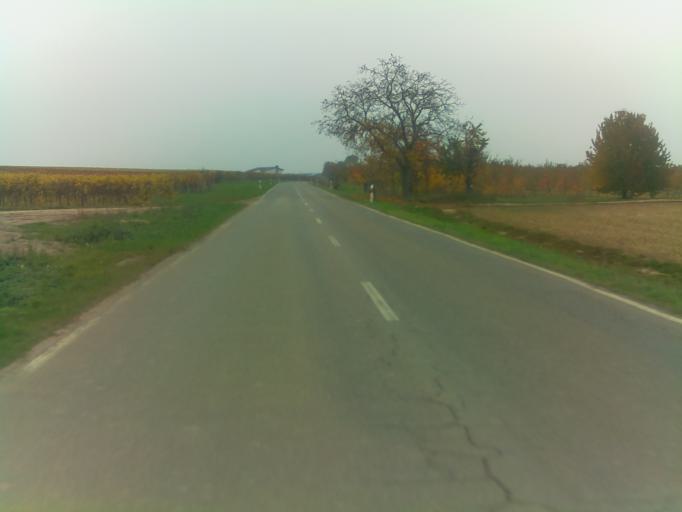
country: DE
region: Rheinland-Pfalz
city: Gonnheim
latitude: 49.4543
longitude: 8.2484
